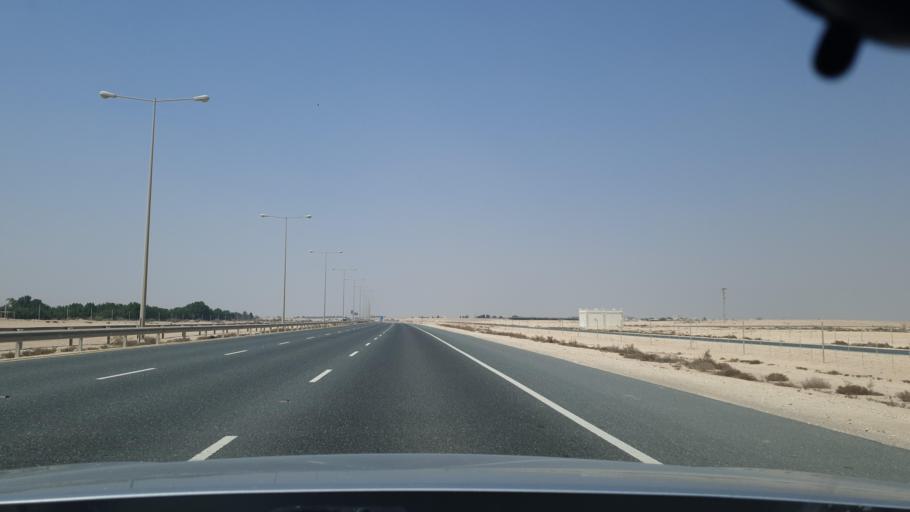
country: QA
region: Al Khawr
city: Al Khawr
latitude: 25.7746
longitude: 51.4102
